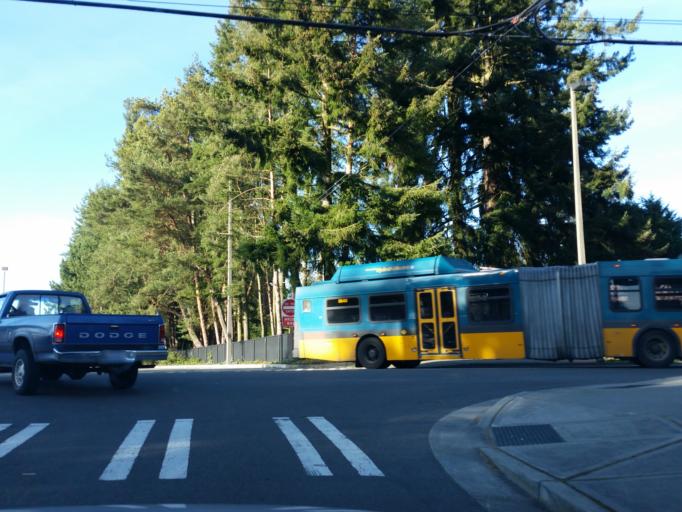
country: US
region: Washington
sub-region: King County
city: Shoreline
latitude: 47.7740
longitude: -122.3406
